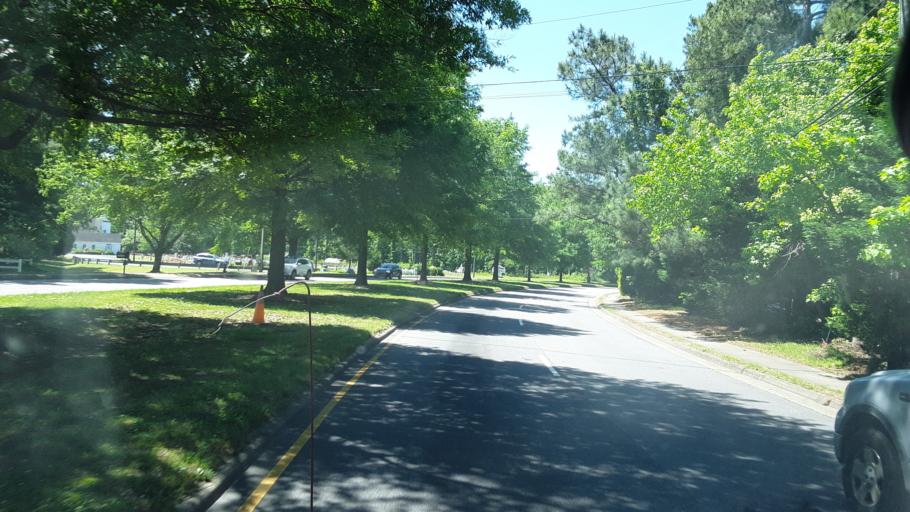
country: US
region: Virginia
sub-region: City of Virginia Beach
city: Virginia Beach
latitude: 36.7624
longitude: -76.0161
